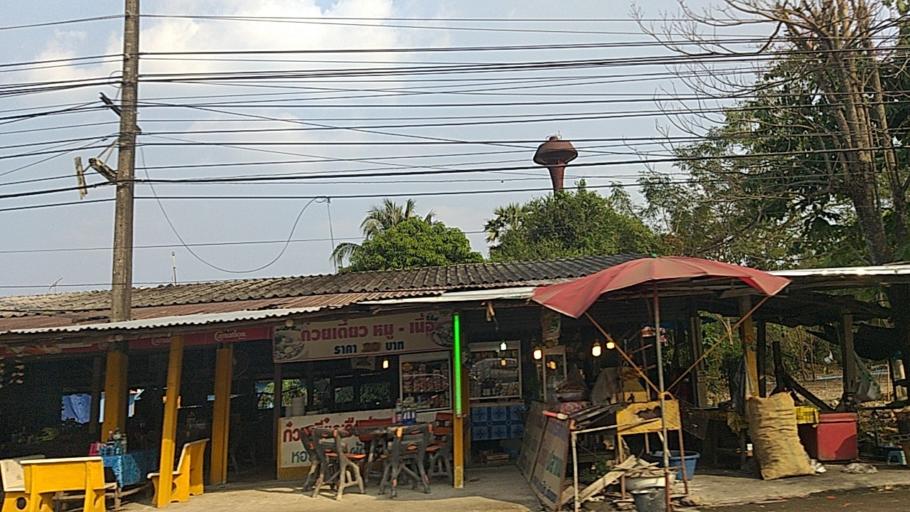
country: TH
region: Nakhon Nayok
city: Nakhon Nayok
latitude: 14.2733
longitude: 101.2739
